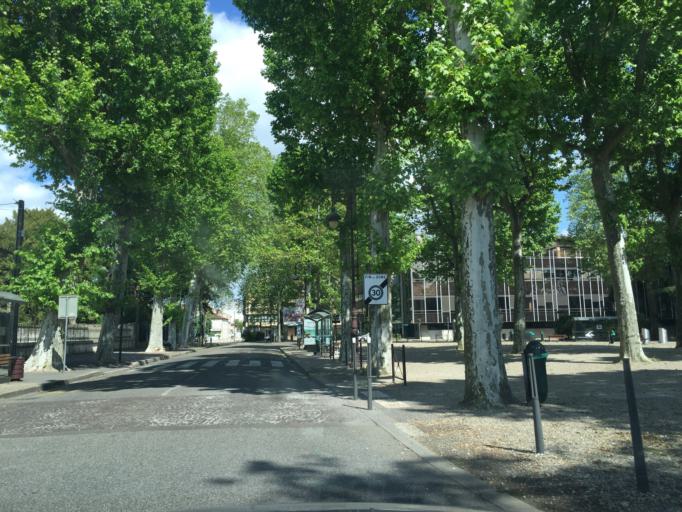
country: FR
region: Aquitaine
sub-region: Departement du Lot-et-Garonne
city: Le Passage
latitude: 44.2006
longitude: 0.6164
